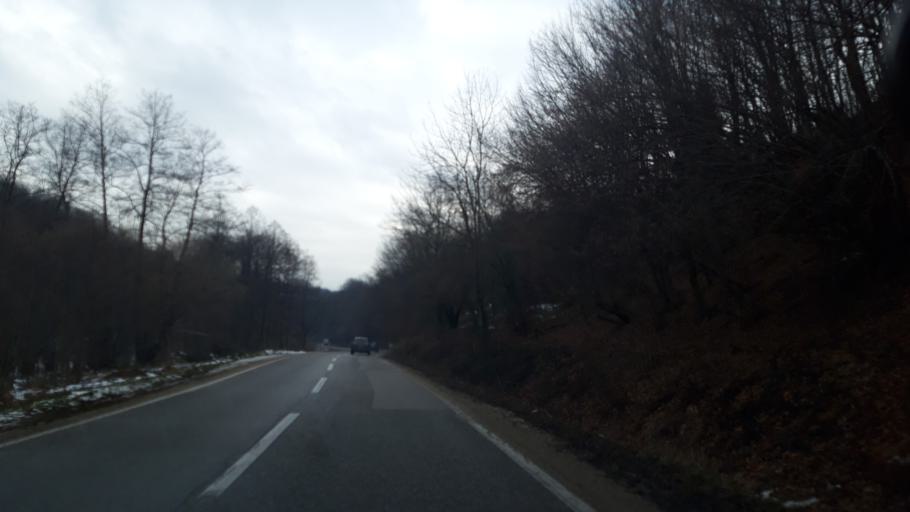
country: BA
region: Republika Srpska
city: Vlasenica
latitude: 44.1751
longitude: 19.0126
